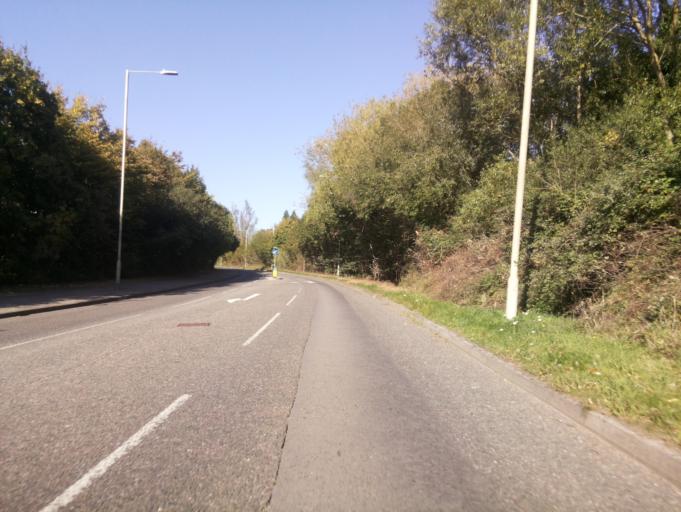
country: GB
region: England
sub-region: West Berkshire
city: Thatcham
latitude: 51.4045
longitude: -1.2418
